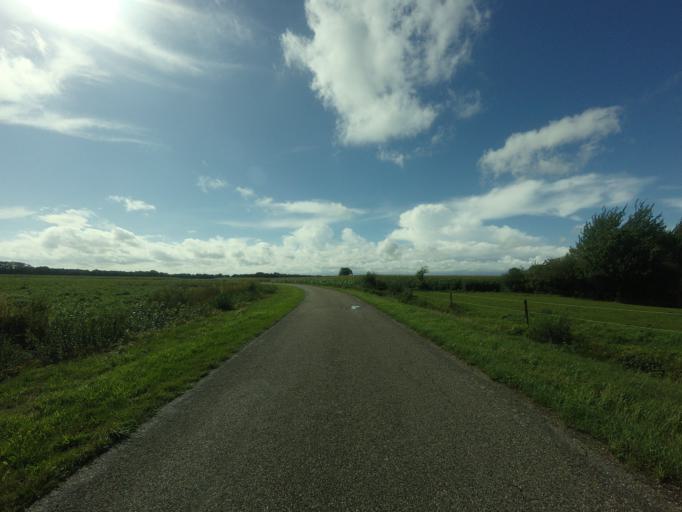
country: NL
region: Groningen
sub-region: Gemeente Leek
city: Leek
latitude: 53.0184
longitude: 6.3070
